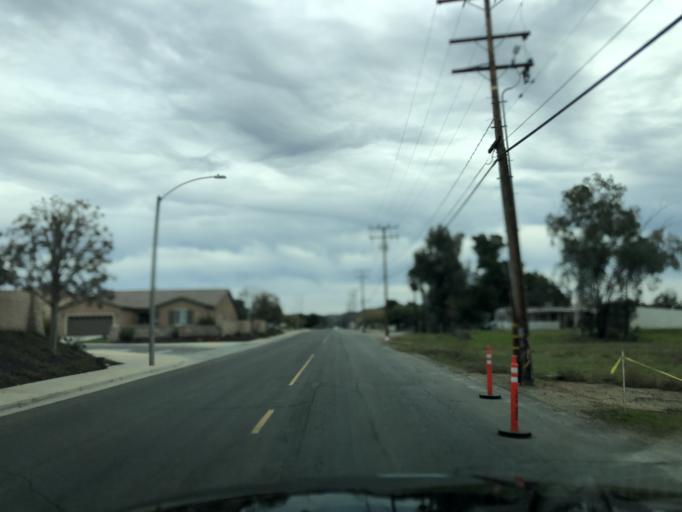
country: US
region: California
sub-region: Riverside County
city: Sedco Hills
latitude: 33.6233
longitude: -117.2876
